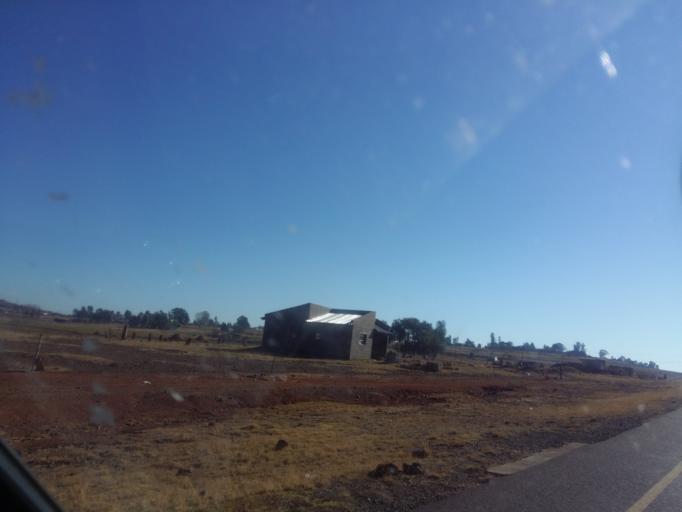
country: LS
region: Mafeteng
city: Mafeteng
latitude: -29.6989
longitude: 27.2901
